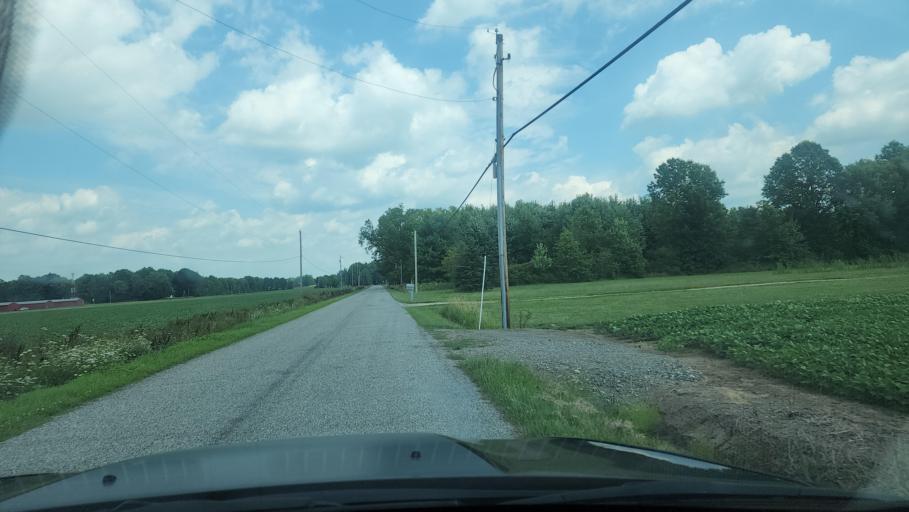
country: US
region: Ohio
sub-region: Trumbull County
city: Leavittsburg
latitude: 41.2678
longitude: -80.9249
